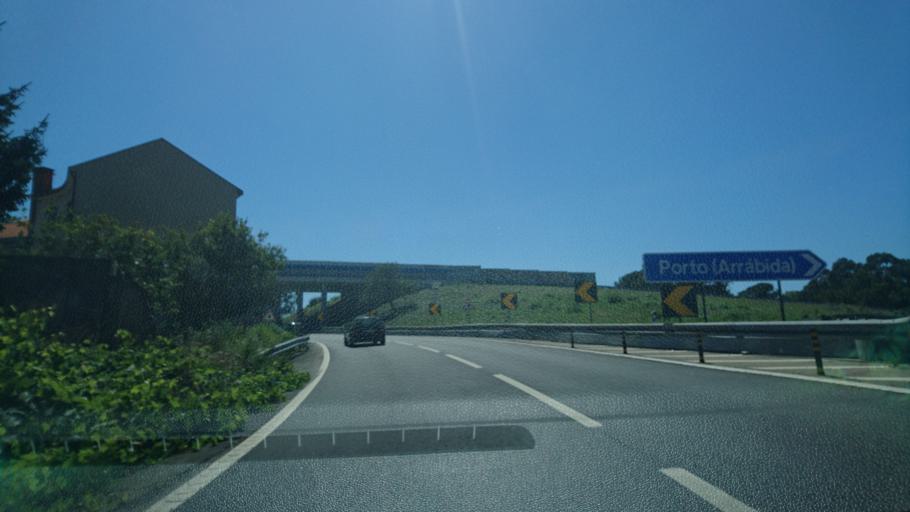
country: PT
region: Porto
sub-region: Vila Nova de Gaia
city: Vila Nova de Gaia
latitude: 41.1172
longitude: -8.6267
